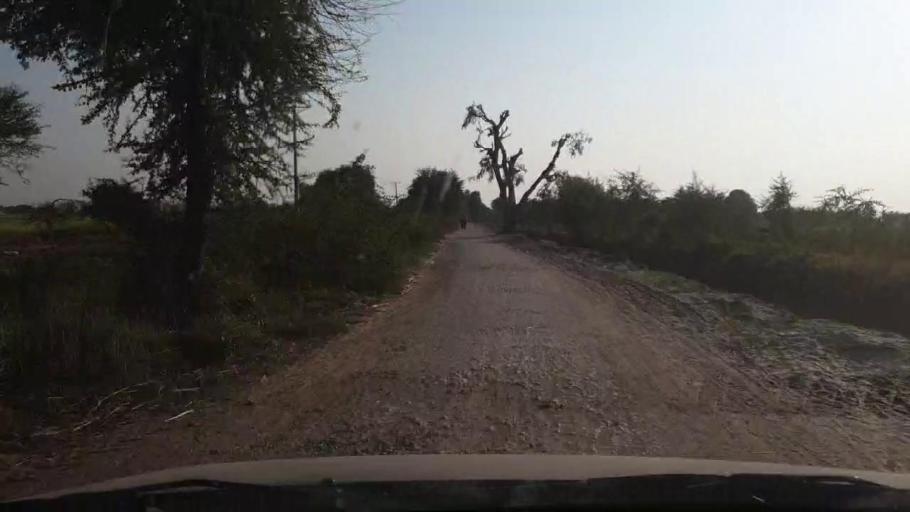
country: PK
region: Sindh
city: Samaro
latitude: 25.2826
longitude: 69.3610
